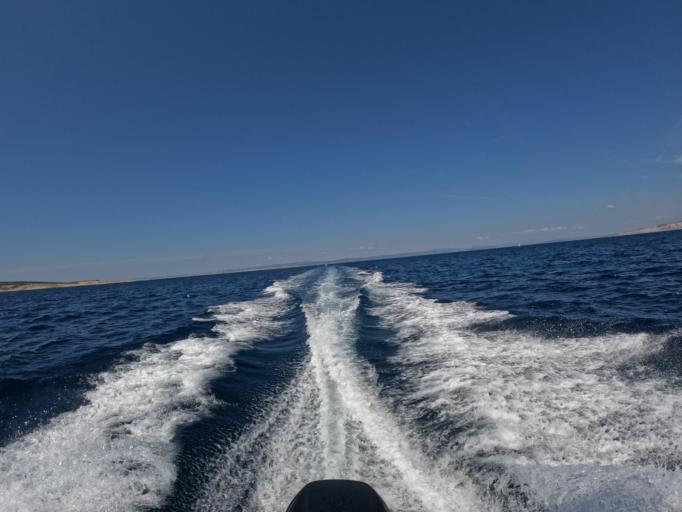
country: HR
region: Primorsko-Goranska
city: Lopar
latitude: 44.8542
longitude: 14.7097
